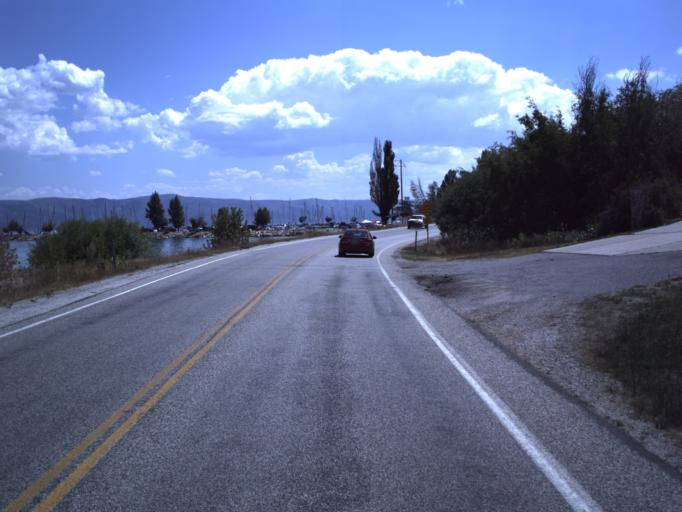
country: US
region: Idaho
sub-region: Bear Lake County
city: Paris
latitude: 41.9680
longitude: -111.4005
